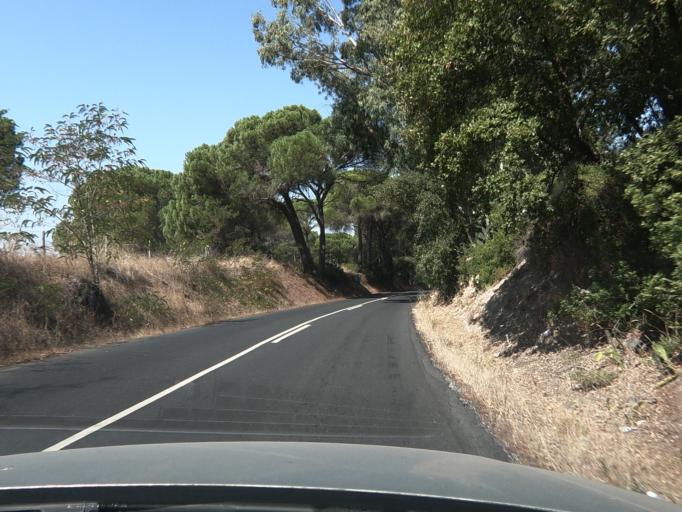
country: PT
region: Setubal
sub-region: Alcacer do Sal
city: Alcacer do Sal
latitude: 38.3522
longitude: -8.4693
